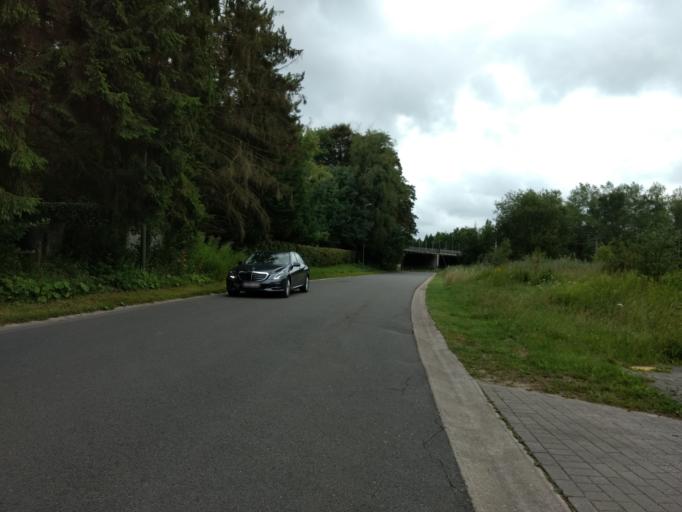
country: BE
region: Flanders
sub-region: Provincie Vlaams-Brabant
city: Oud-Heverlee
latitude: 50.8513
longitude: 4.6721
